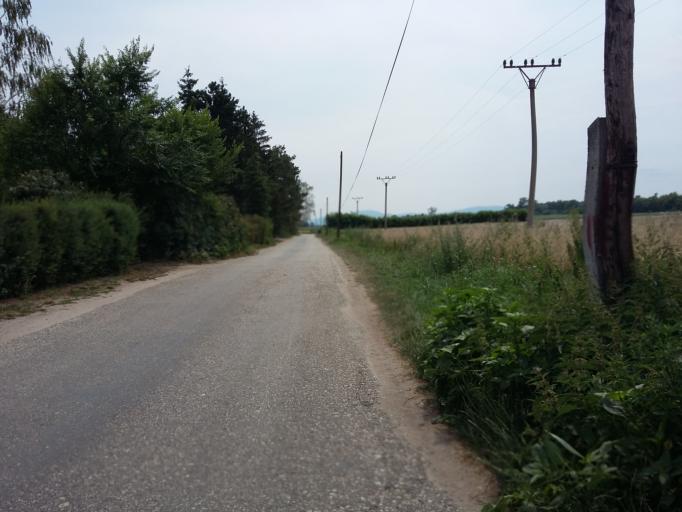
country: AT
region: Lower Austria
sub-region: Politischer Bezirk Ganserndorf
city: Drosing
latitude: 48.4904
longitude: 16.9588
